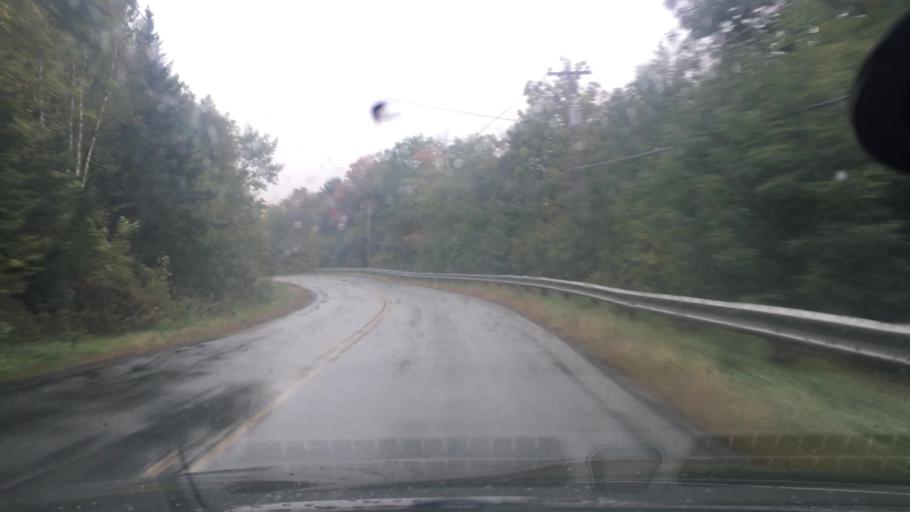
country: CA
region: Nova Scotia
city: Windsor
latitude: 44.8333
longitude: -64.2604
